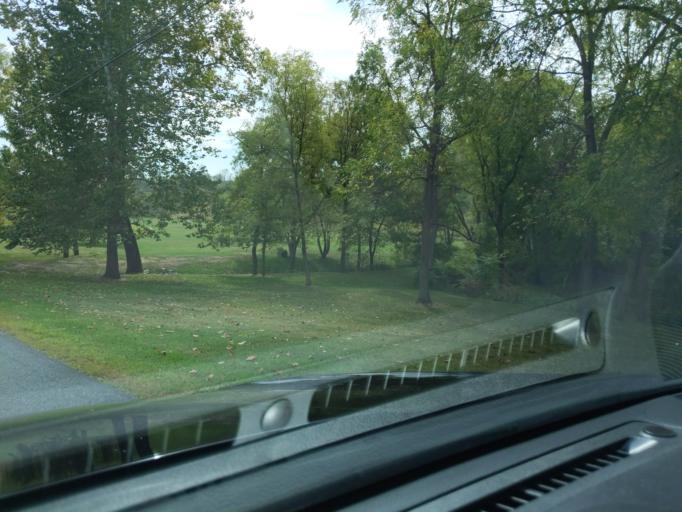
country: US
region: Pennsylvania
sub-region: Blair County
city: Hollidaysburg
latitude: 40.4233
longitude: -78.3452
